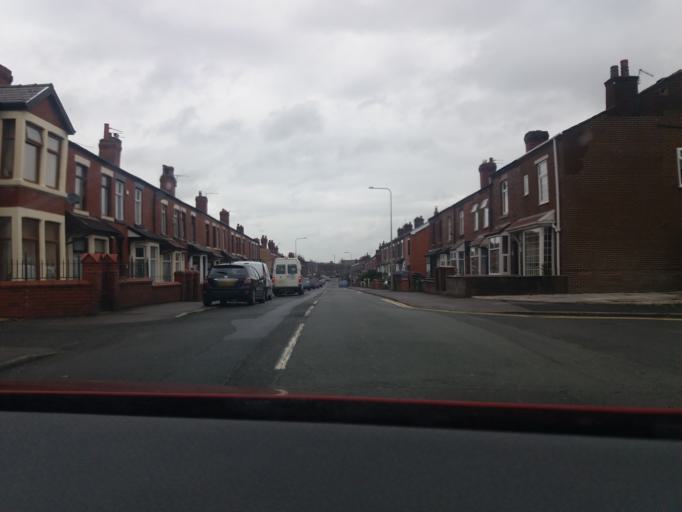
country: GB
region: England
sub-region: Lancashire
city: Chorley
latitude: 53.6443
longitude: -2.6281
